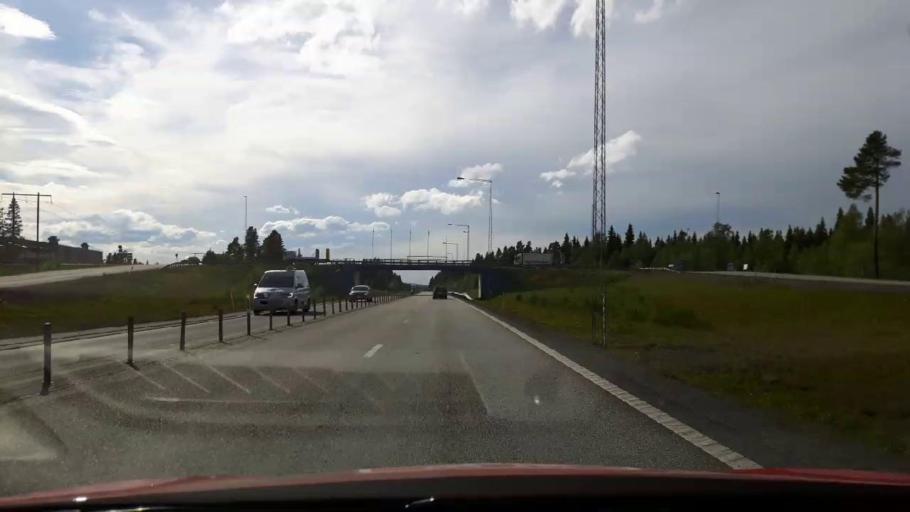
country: SE
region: Jaemtland
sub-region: OEstersunds Kommun
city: Ostersund
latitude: 63.1710
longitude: 14.7052
